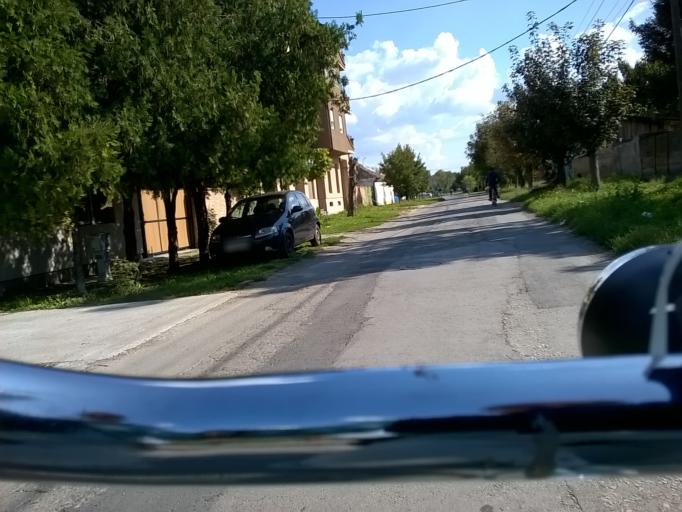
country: RS
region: Autonomna Pokrajina Vojvodina
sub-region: Juznobanatski Okrug
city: Pancevo
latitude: 44.8828
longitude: 20.6383
